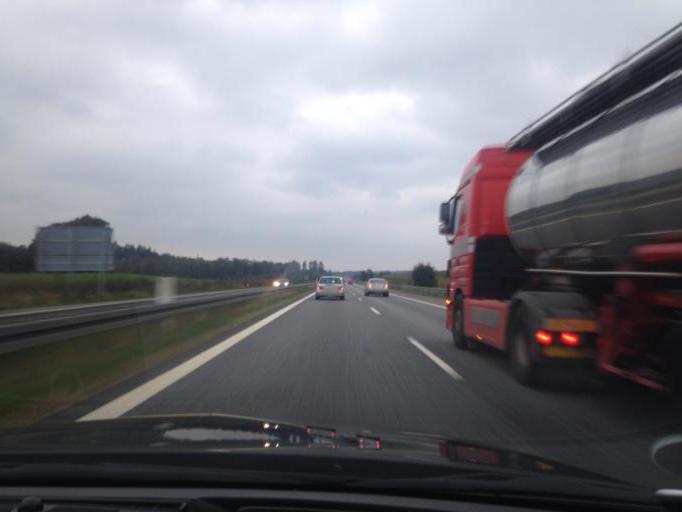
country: DK
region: South Denmark
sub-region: Haderslev Kommune
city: Haderslev
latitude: 55.2574
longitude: 9.4105
